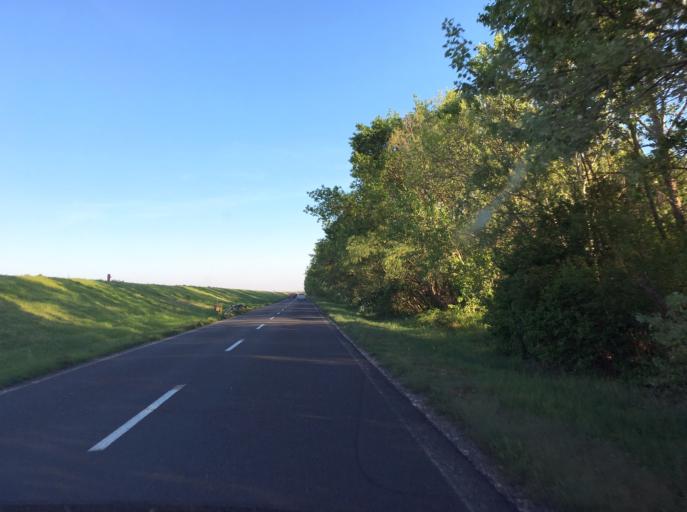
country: HU
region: Gyor-Moson-Sopron
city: Rajka
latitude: 48.0238
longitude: 17.2455
